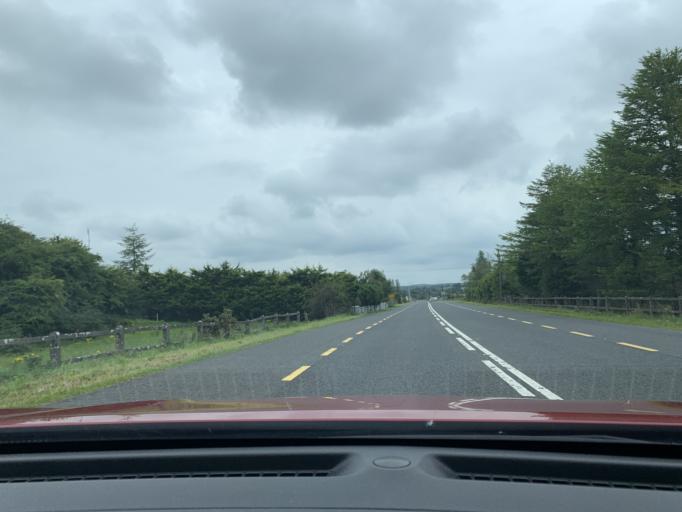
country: IE
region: Connaught
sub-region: Maigh Eo
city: Swinford
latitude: 53.8643
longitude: -8.8541
